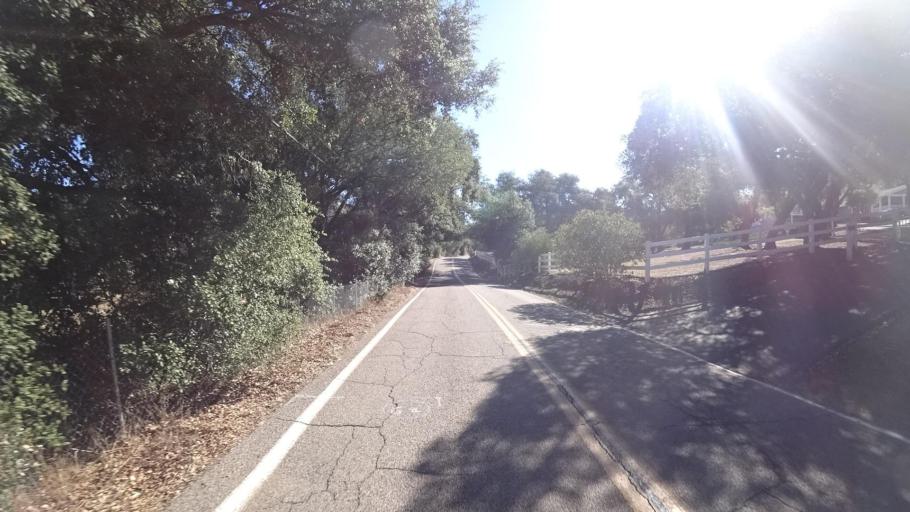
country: US
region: California
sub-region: San Diego County
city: Jamul
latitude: 32.7155
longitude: -116.7659
